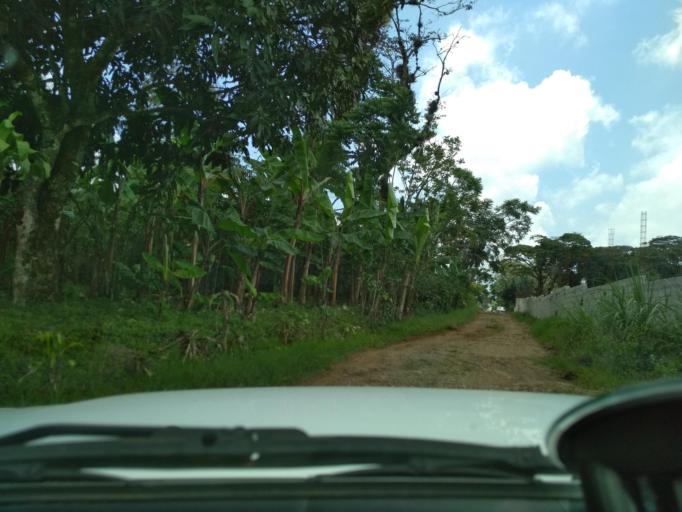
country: MX
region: Veracruz
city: Tocuila
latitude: 18.9495
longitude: -97.0194
